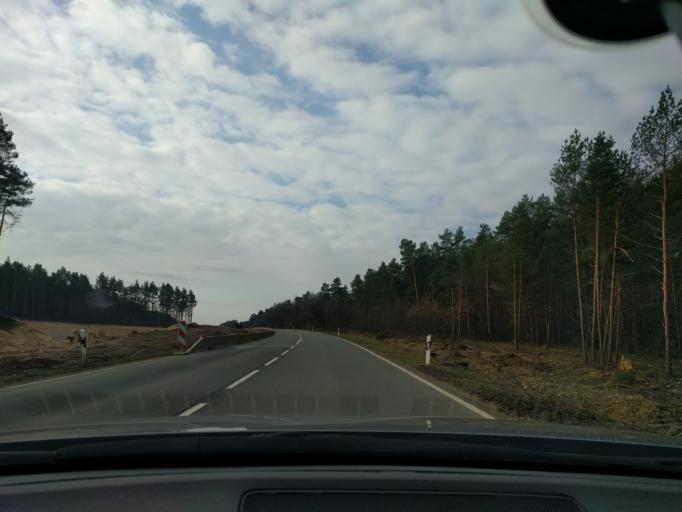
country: DE
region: Saxony-Anhalt
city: Colbitz
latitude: 52.3660
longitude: 11.6129
